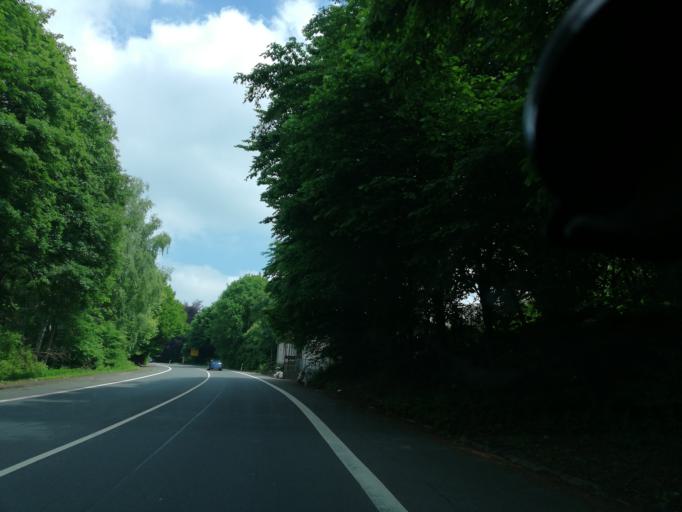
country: DE
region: North Rhine-Westphalia
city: Herdecke
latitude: 51.4242
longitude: 7.4630
